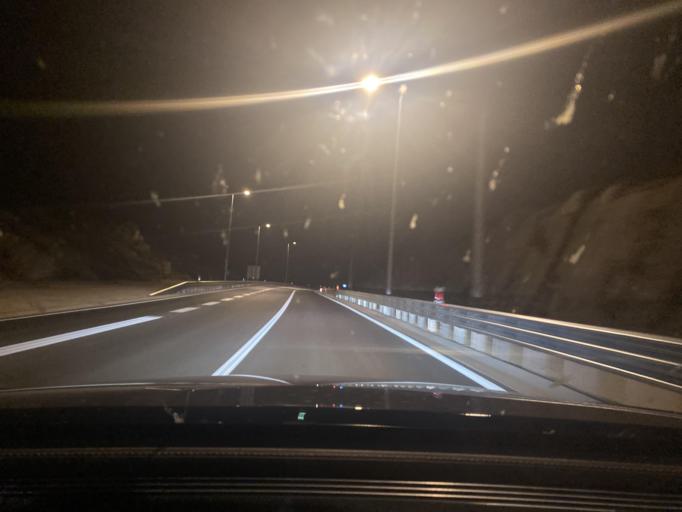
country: BA
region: Federation of Bosnia and Herzegovina
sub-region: Hercegovacko-Bosanski Kanton
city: Neum
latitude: 42.9190
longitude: 17.5270
